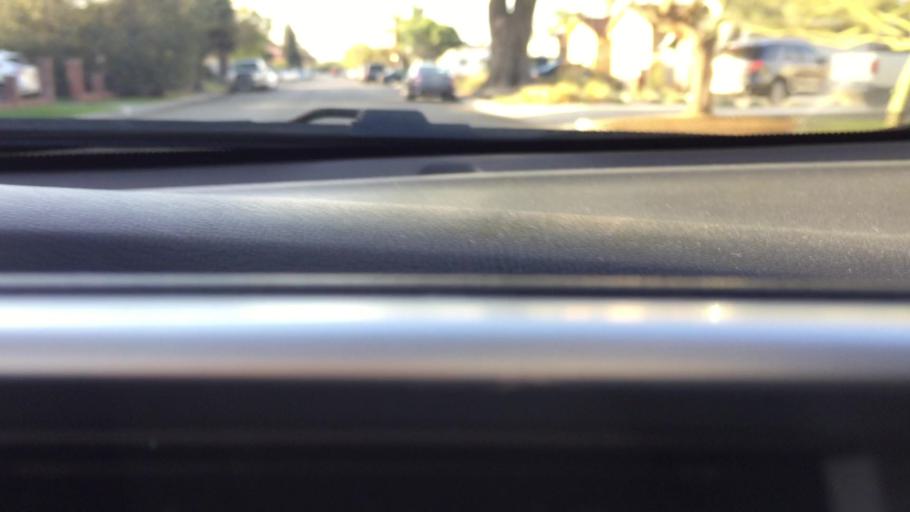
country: US
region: California
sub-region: Orange County
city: Garden Grove
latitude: 33.8055
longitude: -117.9563
